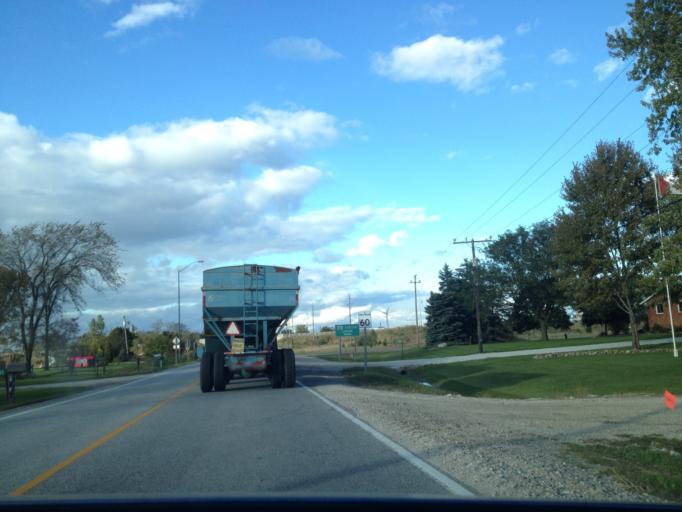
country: US
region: Michigan
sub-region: Wayne County
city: Grosse Pointe Farms
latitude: 42.2344
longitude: -82.7130
